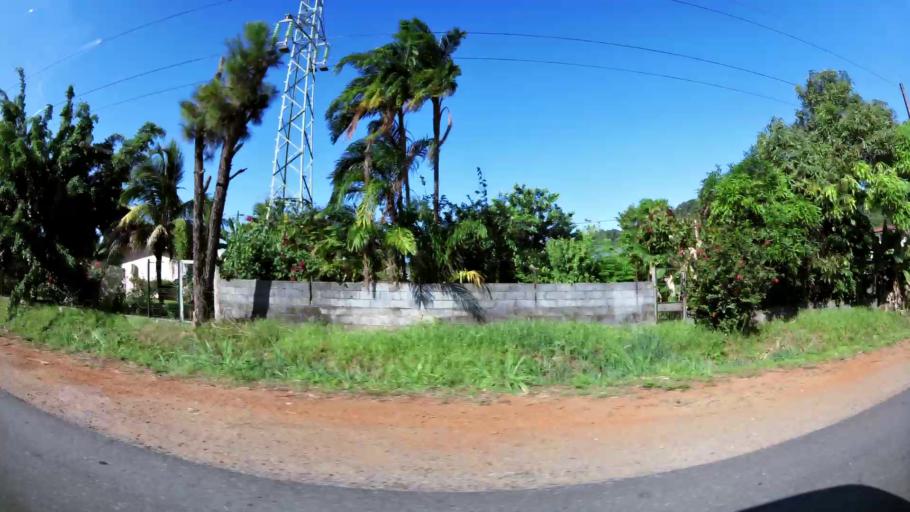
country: GF
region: Guyane
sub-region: Guyane
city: Remire-Montjoly
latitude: 4.8806
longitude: -52.2802
